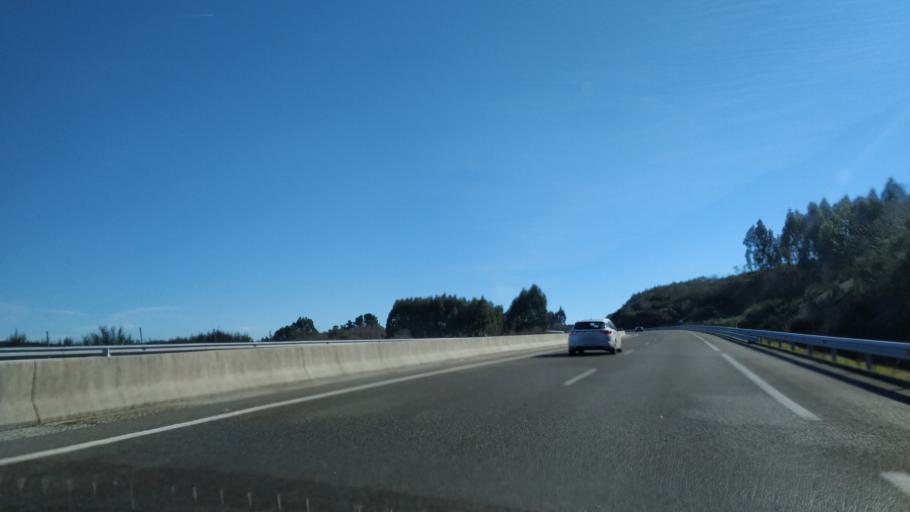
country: ES
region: Galicia
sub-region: Provincia de Pontevedra
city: Dozon
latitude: 42.5647
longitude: -8.0440
